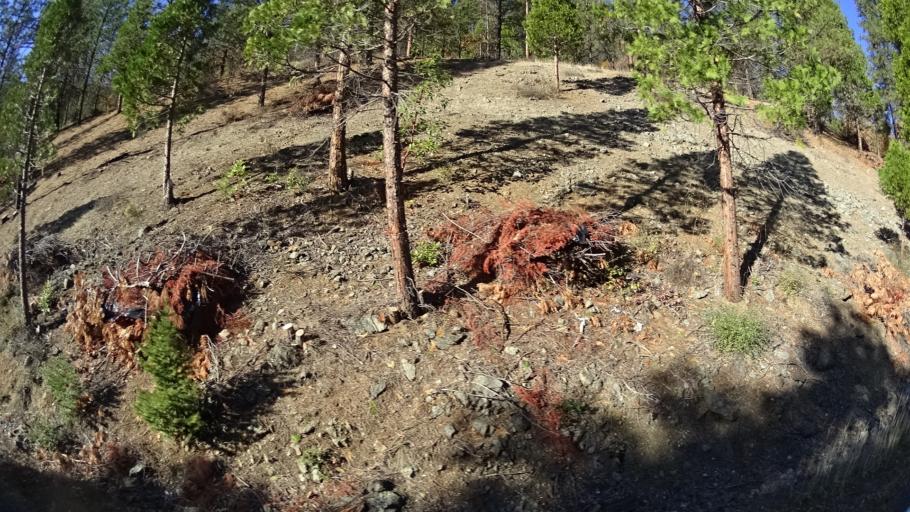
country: US
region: California
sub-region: Siskiyou County
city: Yreka
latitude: 41.8968
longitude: -122.8262
